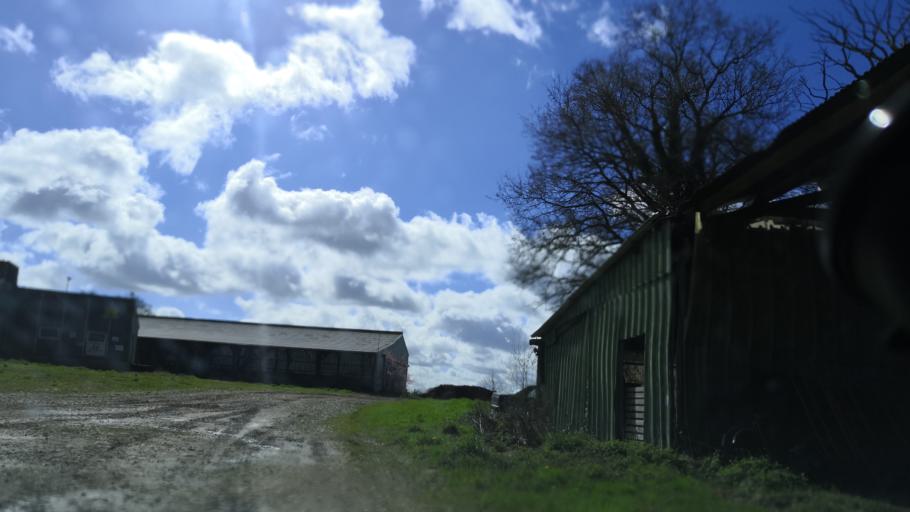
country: FR
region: Brittany
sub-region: Departement d'Ille-et-Vilaine
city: Bedee
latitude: 48.1815
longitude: -1.9748
